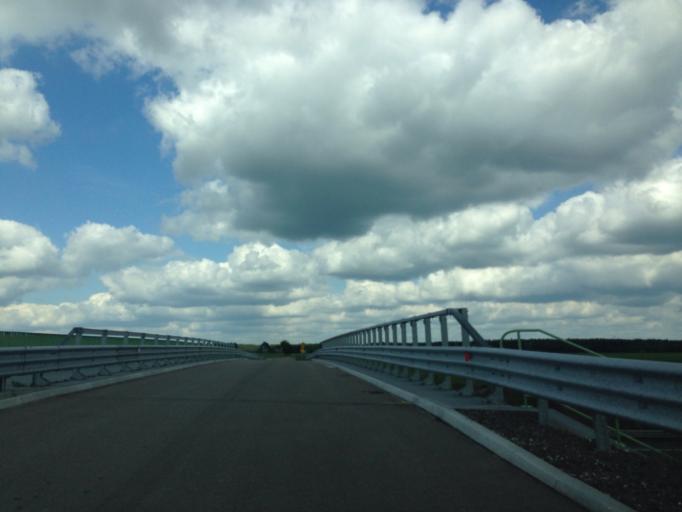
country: PL
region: Warmian-Masurian Voivodeship
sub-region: Powiat nidzicki
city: Nidzica
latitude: 53.4425
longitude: 20.3360
